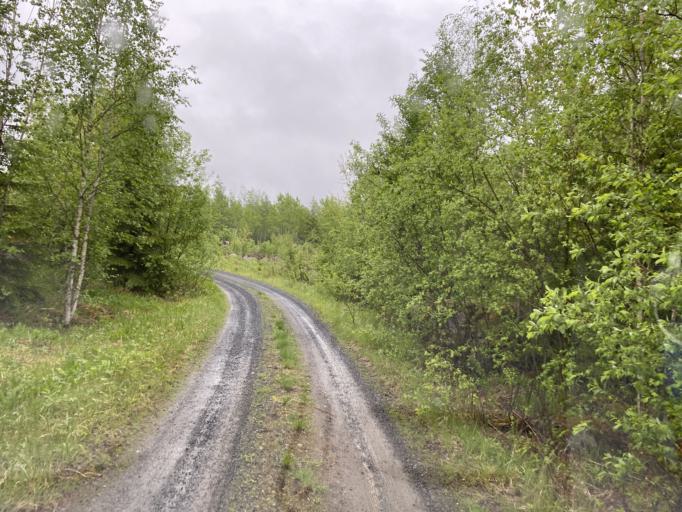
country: FI
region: Pirkanmaa
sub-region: Etelae-Pirkanmaa
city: Urjala
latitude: 60.9536
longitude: 23.5572
